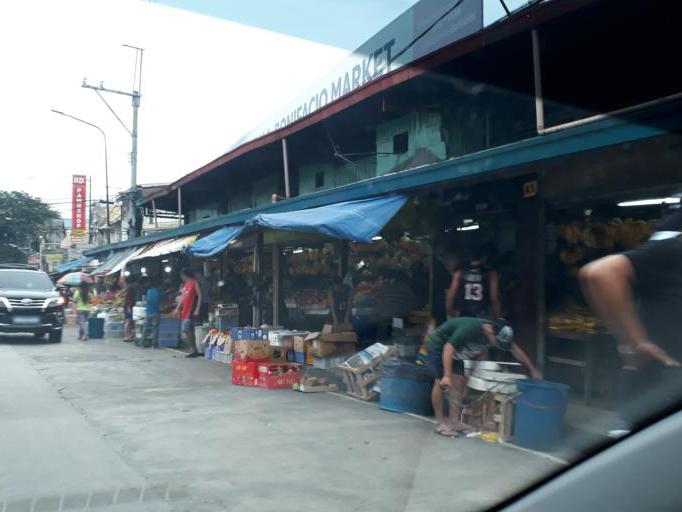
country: PH
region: Calabarzon
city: Del Monte
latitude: 14.6367
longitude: 120.9938
